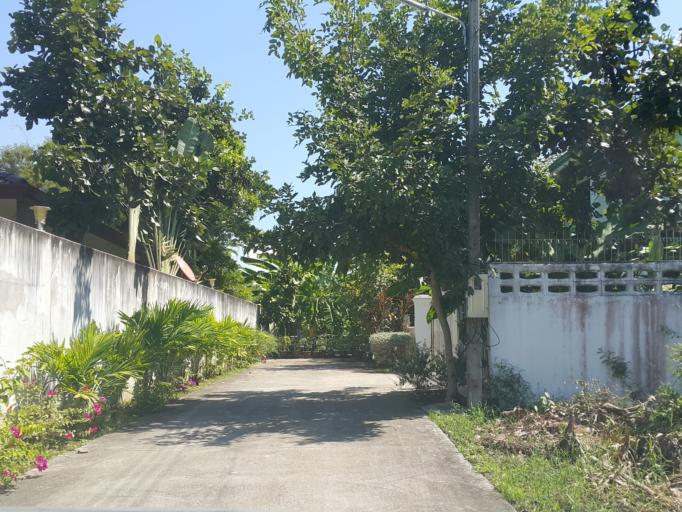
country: TH
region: Chiang Mai
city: Saraphi
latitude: 18.7588
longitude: 99.0565
